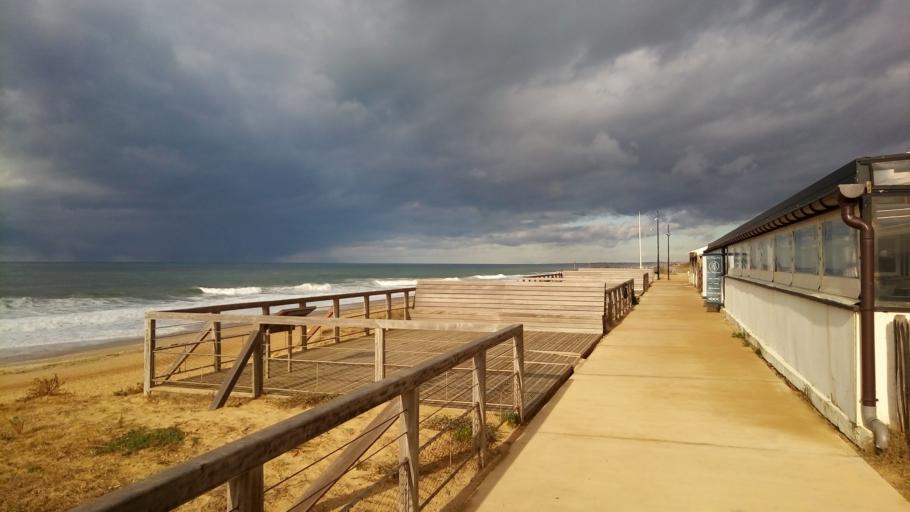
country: FR
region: Aquitaine
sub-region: Departement des Landes
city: Tarnos
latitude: 43.5767
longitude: -1.4880
